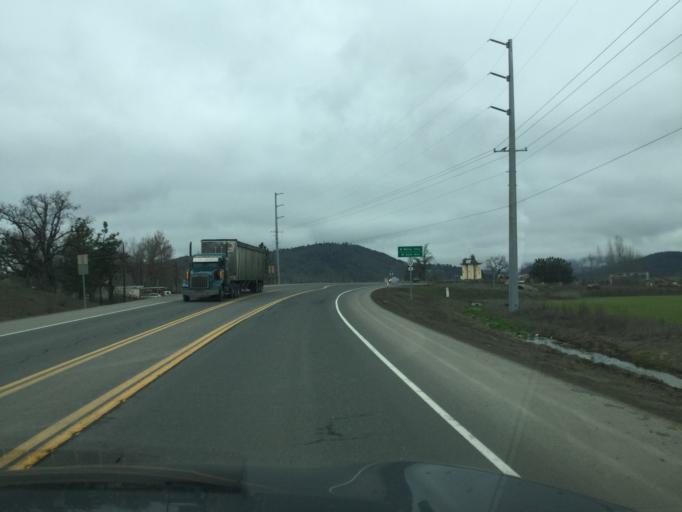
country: US
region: Oregon
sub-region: Jackson County
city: Central Point
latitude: 42.4198
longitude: -122.9554
